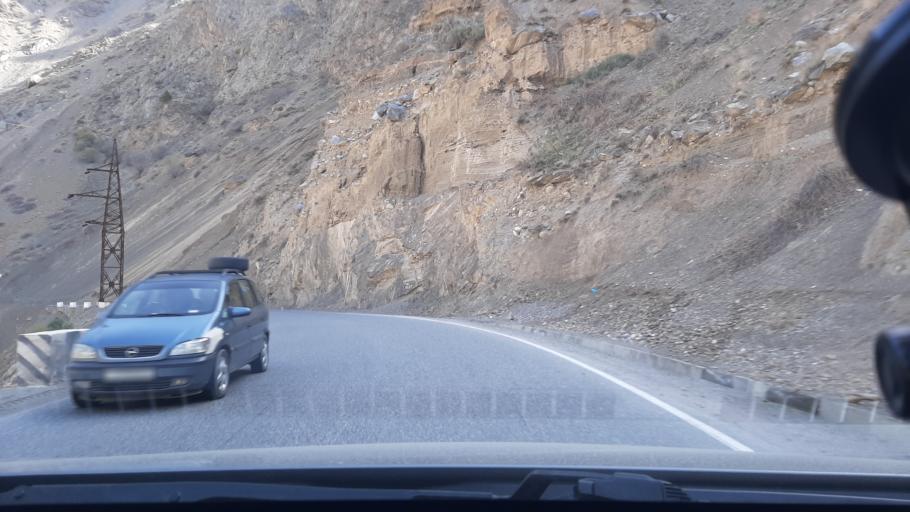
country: TJ
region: Viloyati Sughd
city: Ayni
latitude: 39.3320
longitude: 68.5532
